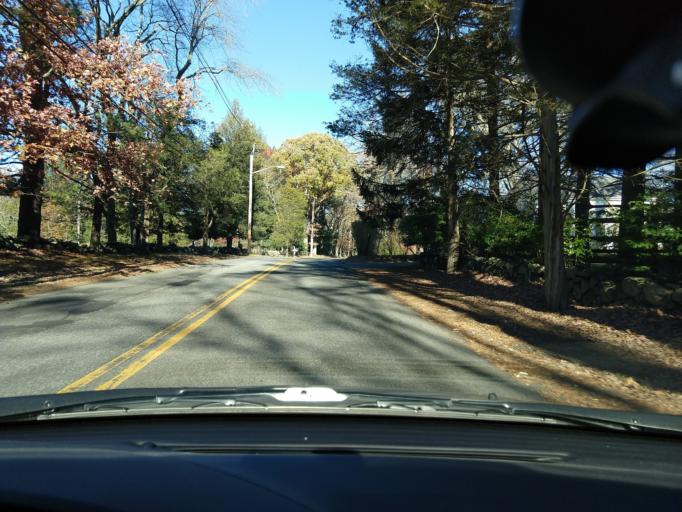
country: US
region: Massachusetts
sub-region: Middlesex County
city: Concord
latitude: 42.4854
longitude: -71.3371
